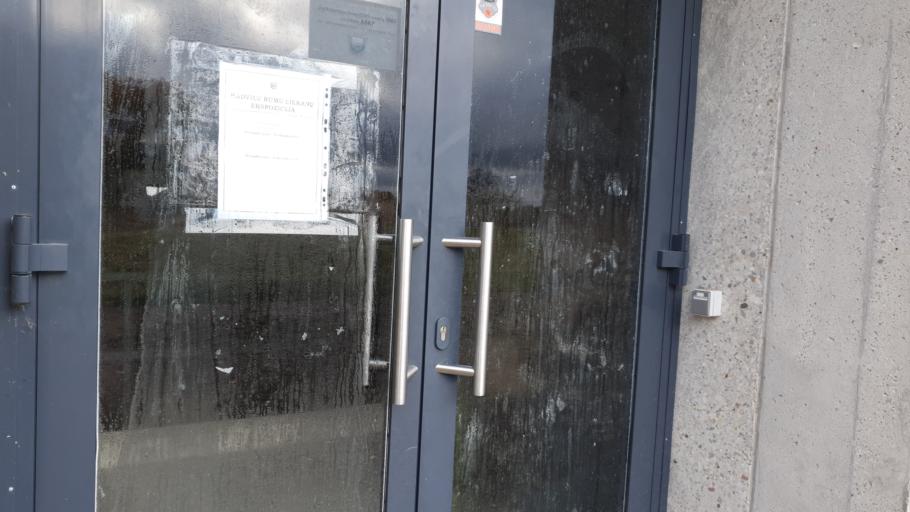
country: LT
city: Moletai
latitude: 55.0595
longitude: 25.4440
